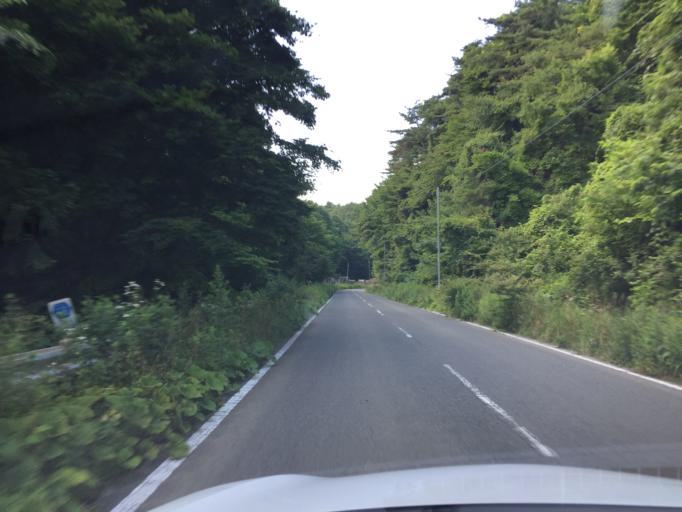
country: JP
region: Fukushima
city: Ishikawa
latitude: 37.1578
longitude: 140.6309
